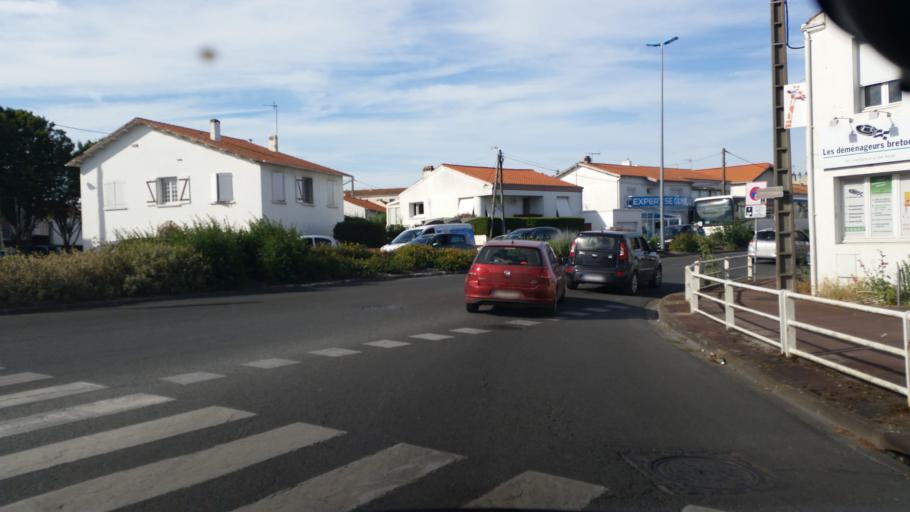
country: FR
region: Poitou-Charentes
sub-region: Departement de la Charente-Maritime
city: La Rochelle
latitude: 46.1665
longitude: -1.1368
